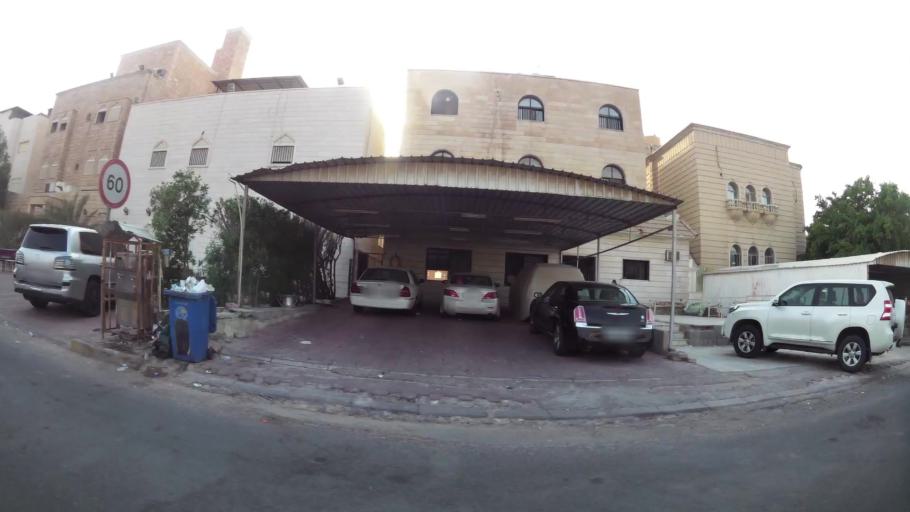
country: KW
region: Mubarak al Kabir
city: Mubarak al Kabir
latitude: 29.1899
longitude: 48.0705
